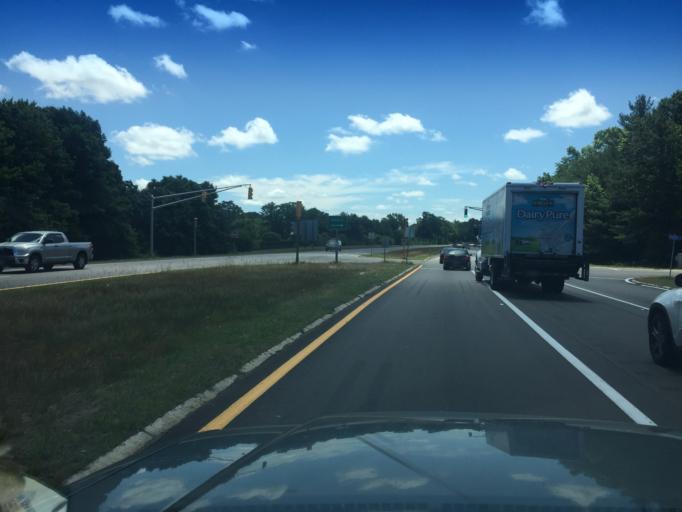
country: US
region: Massachusetts
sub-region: Bristol County
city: Mansfield
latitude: 42.0394
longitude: -71.2384
